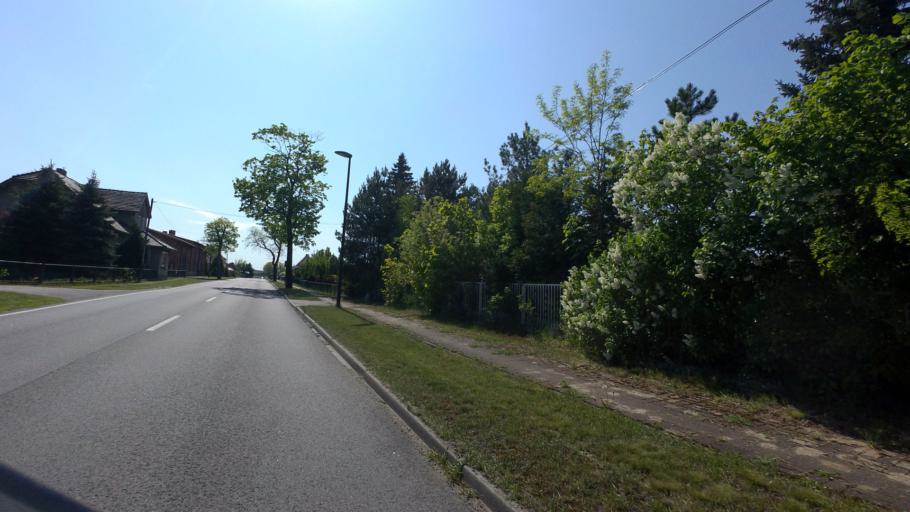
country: DE
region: Brandenburg
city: Neu Zauche
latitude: 52.0298
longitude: 14.0920
